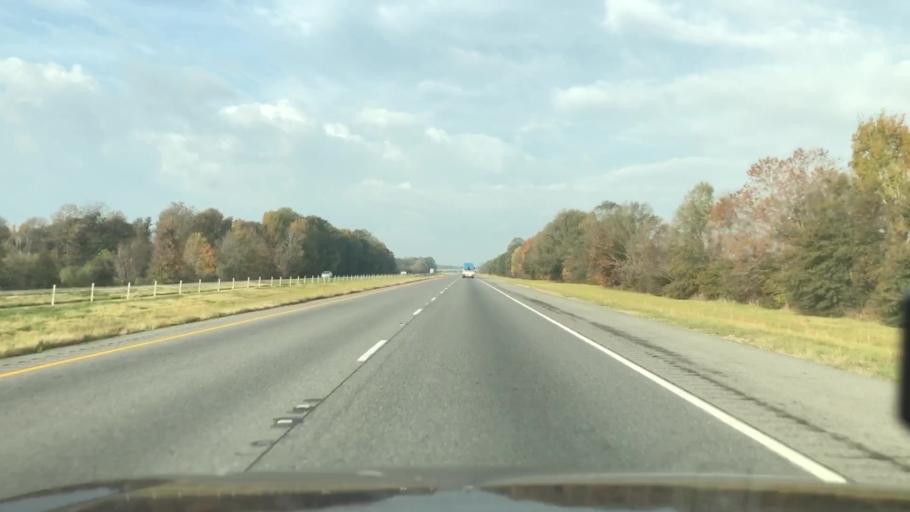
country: US
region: Louisiana
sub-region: Richland Parish
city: Delhi
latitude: 32.4235
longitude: -91.3531
